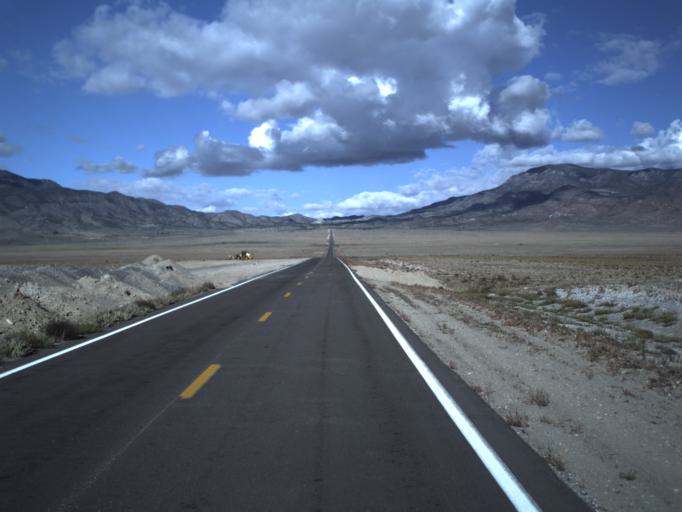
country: US
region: Utah
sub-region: Beaver County
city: Milford
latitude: 38.4777
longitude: -113.4292
